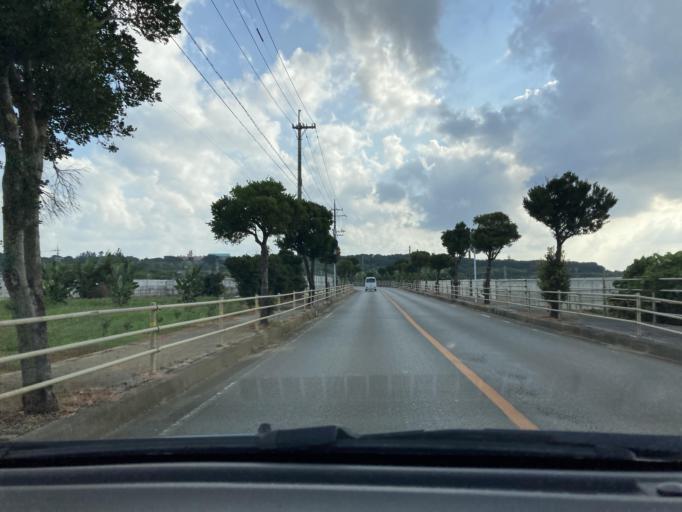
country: JP
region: Okinawa
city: Itoman
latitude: 26.1016
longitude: 127.6663
